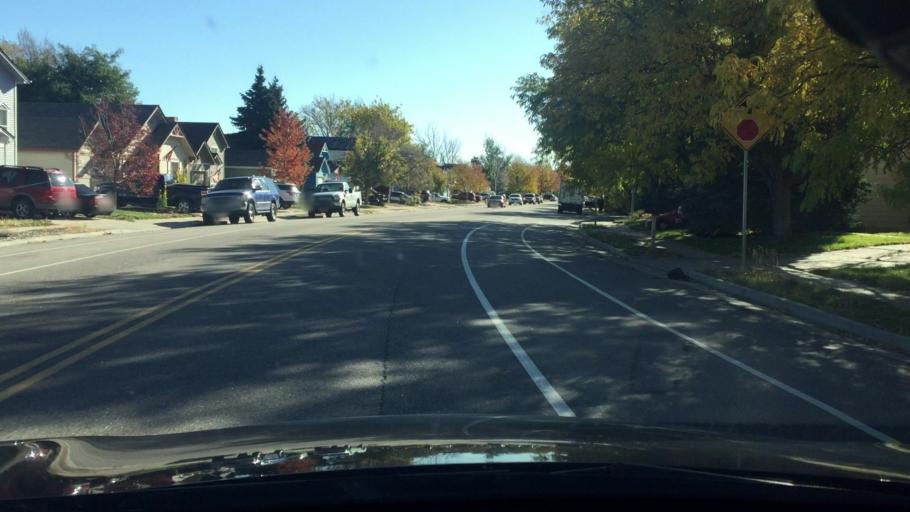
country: US
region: Colorado
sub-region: Arapahoe County
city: Dove Valley
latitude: 39.6306
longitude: -104.7899
